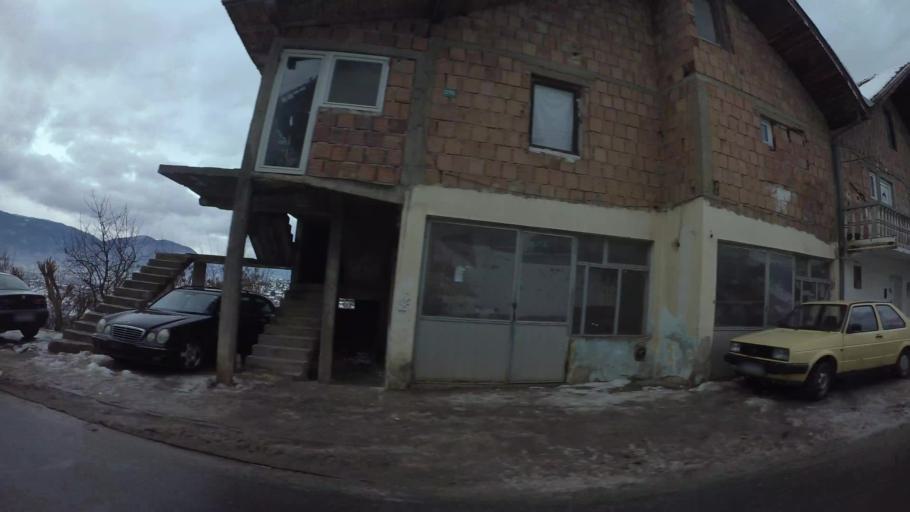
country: BA
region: Federation of Bosnia and Herzegovina
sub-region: Kanton Sarajevo
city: Sarajevo
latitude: 43.8615
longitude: 18.3537
